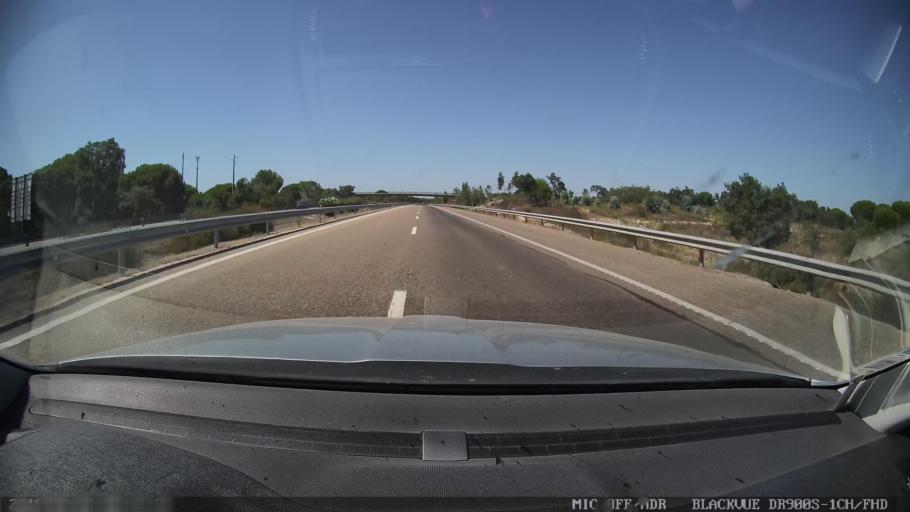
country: PT
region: Evora
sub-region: Vendas Novas
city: Vendas Novas
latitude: 38.6371
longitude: -8.5101
